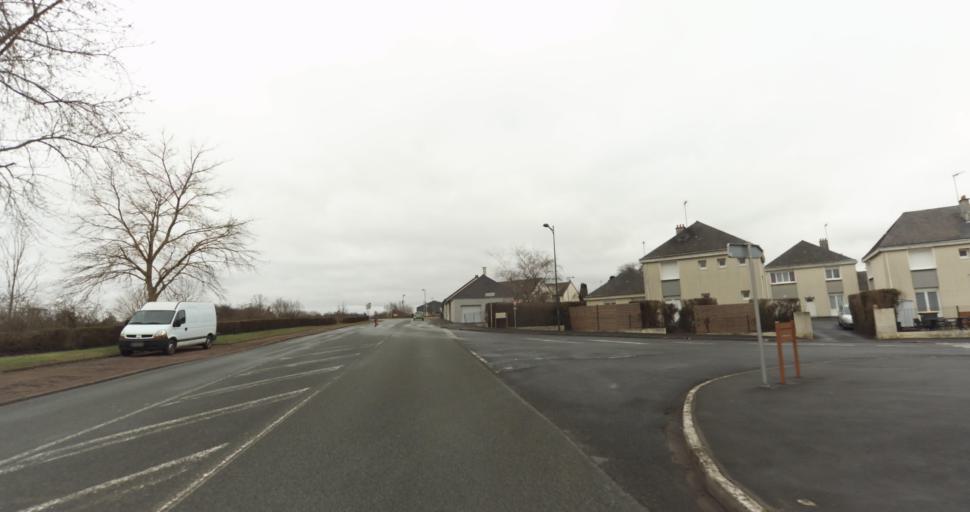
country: FR
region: Pays de la Loire
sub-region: Departement de Maine-et-Loire
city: Montreuil-Bellay
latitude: 47.1289
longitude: -0.1495
